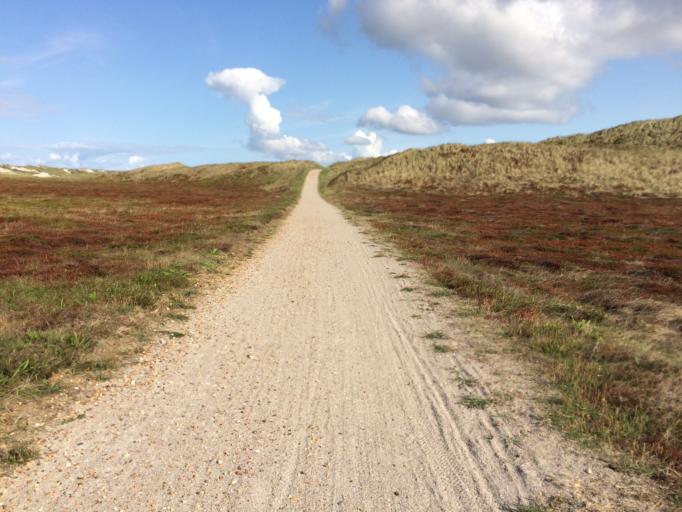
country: DK
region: Central Jutland
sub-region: Ringkobing-Skjern Kommune
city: Hvide Sande
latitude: 55.8972
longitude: 8.1601
